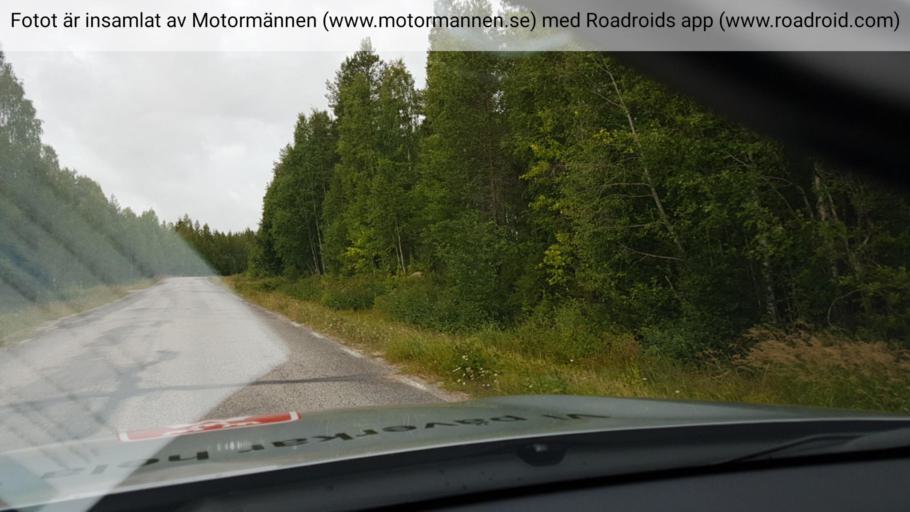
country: SE
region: Norrbotten
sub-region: Bodens Kommun
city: Saevast
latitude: 65.6684
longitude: 21.7326
